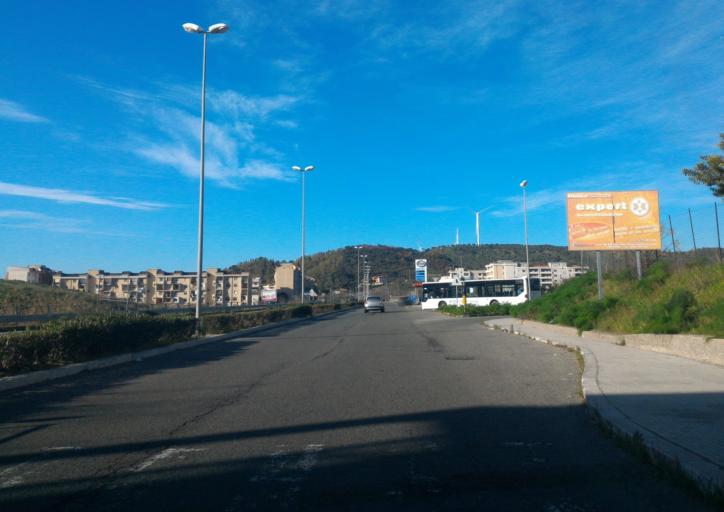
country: IT
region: Calabria
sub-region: Provincia di Crotone
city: Crotone
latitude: 39.0646
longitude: 17.1101
